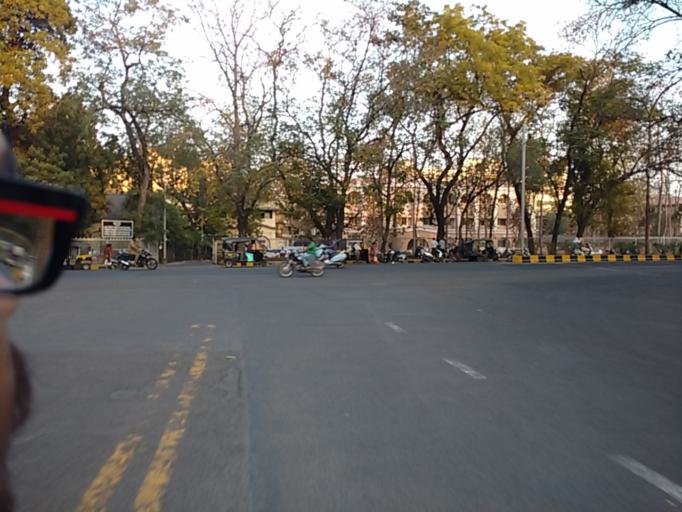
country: IN
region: Maharashtra
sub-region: Nagpur Division
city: Nagpur
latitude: 21.1580
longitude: 79.0685
